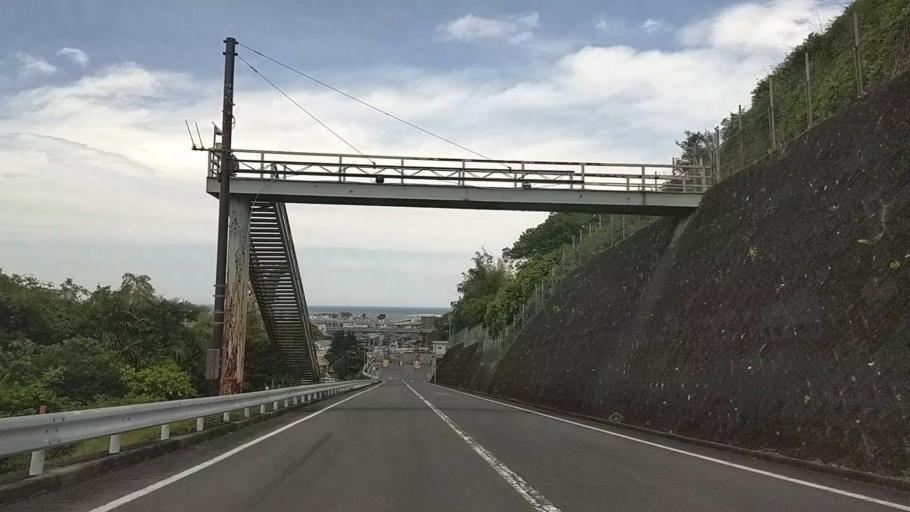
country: JP
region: Kanagawa
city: Odawara
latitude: 35.2424
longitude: 139.1382
